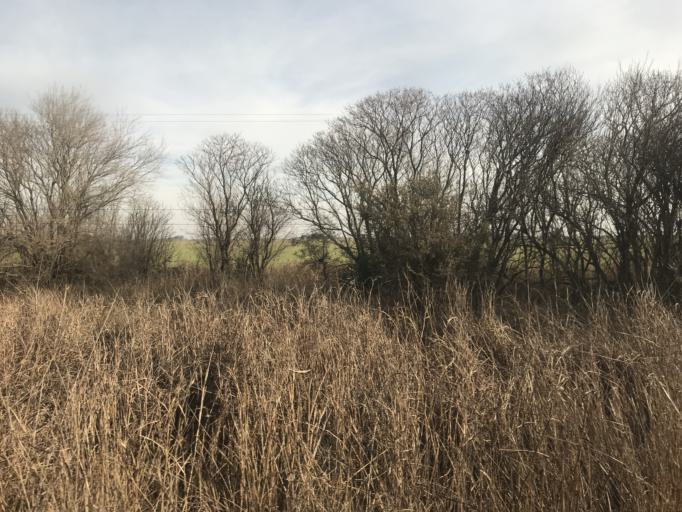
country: AR
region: Cordoba
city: Laguna Larga
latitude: -31.7609
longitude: -63.8169
